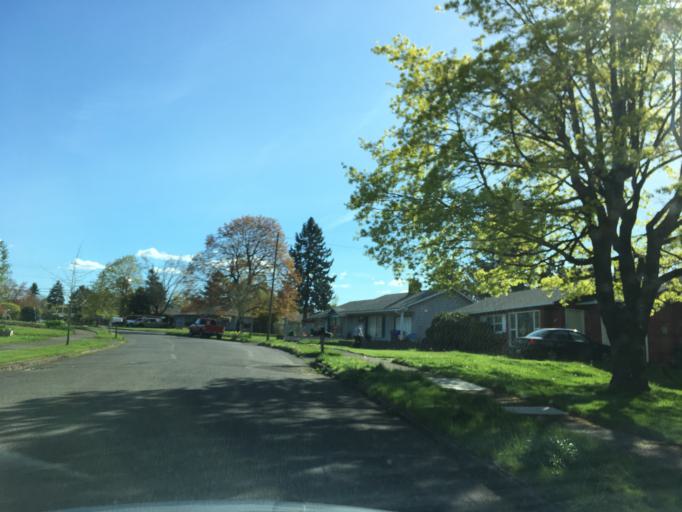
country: US
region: Oregon
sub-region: Multnomah County
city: Lents
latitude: 45.5419
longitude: -122.5201
